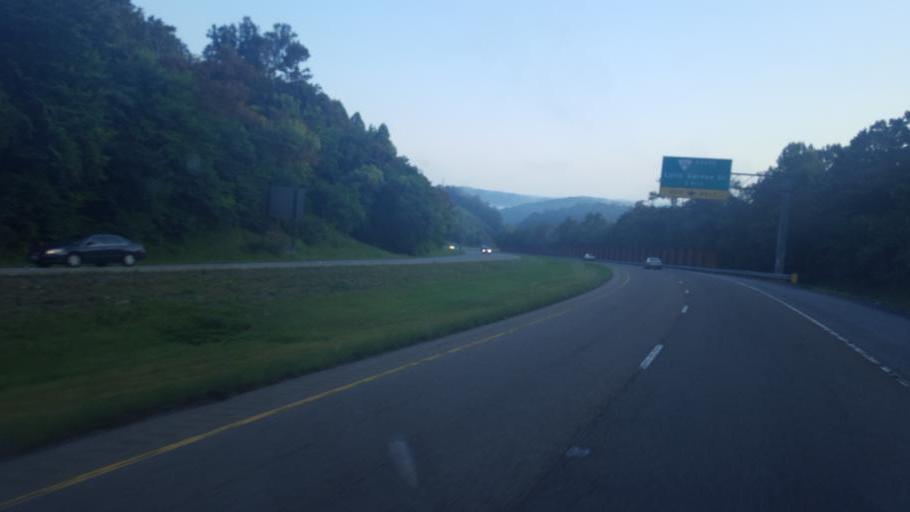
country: US
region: Tennessee
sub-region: Sullivan County
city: Kingsport
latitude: 36.5781
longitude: -82.5788
